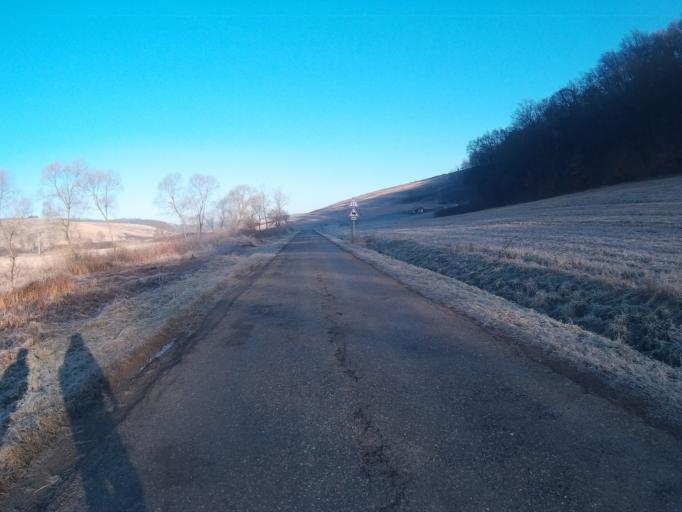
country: HU
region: Borsod-Abauj-Zemplen
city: Putnok
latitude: 48.3636
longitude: 20.4287
